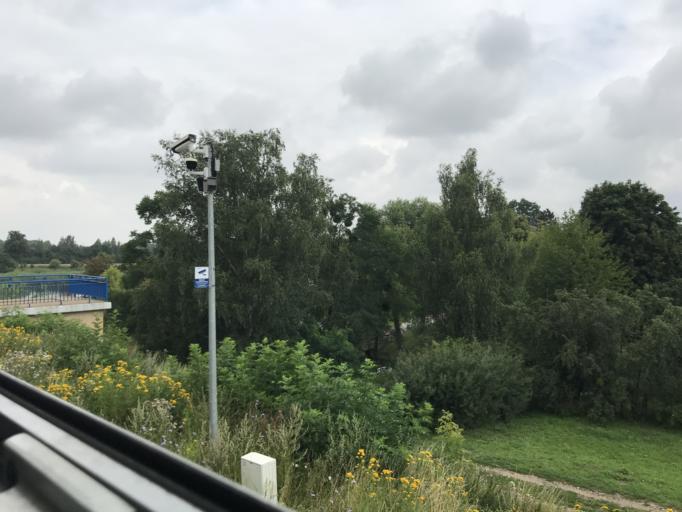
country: PL
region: Pomeranian Voivodeship
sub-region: Powiat malborski
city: Malbork
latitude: 54.0433
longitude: 19.0318
